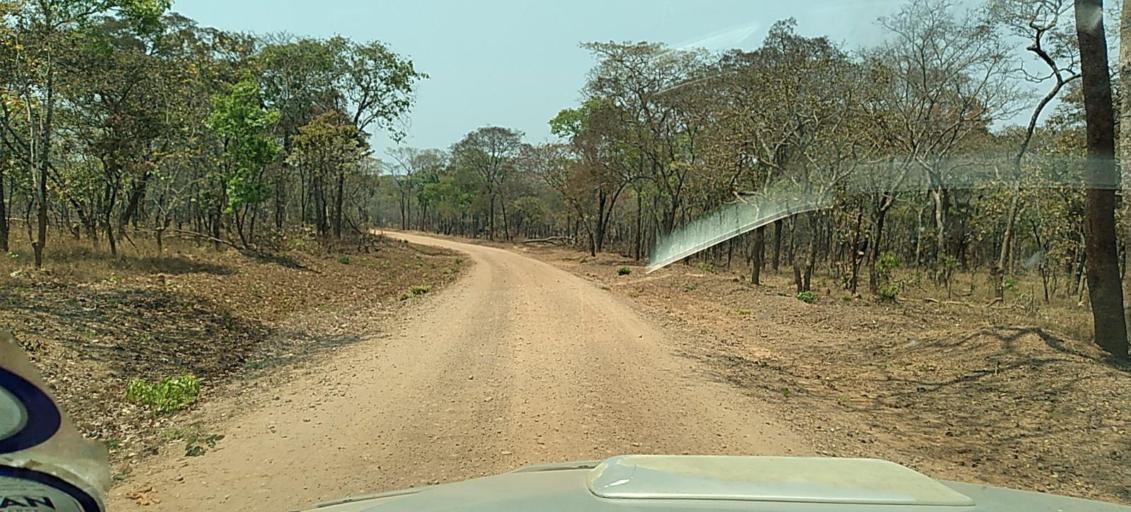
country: ZM
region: North-Western
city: Kasempa
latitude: -13.5471
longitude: 26.0508
